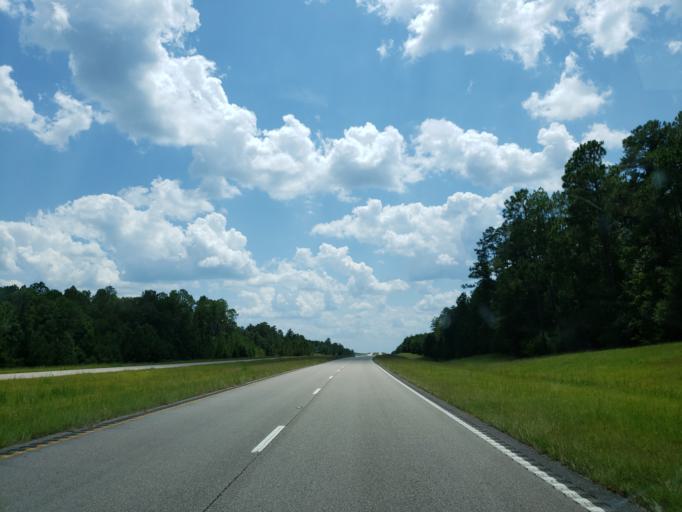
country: US
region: Mississippi
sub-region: Greene County
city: Leakesville
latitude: 31.1447
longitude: -88.5024
